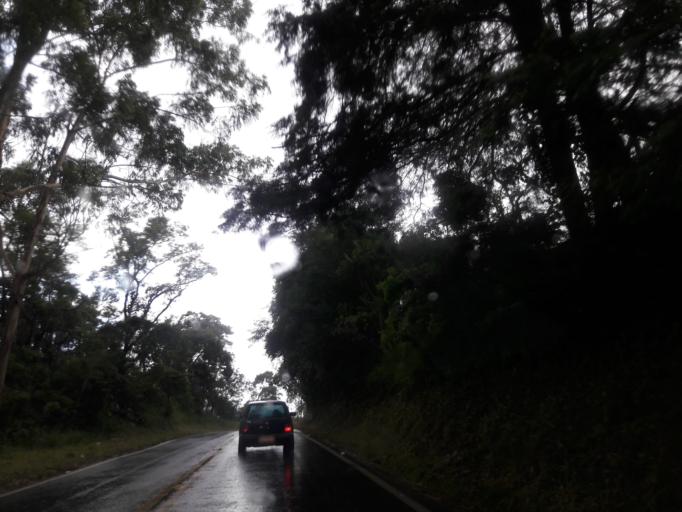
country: BR
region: Sao Paulo
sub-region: Aruja
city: Aruja
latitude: -23.2913
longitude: -46.4268
